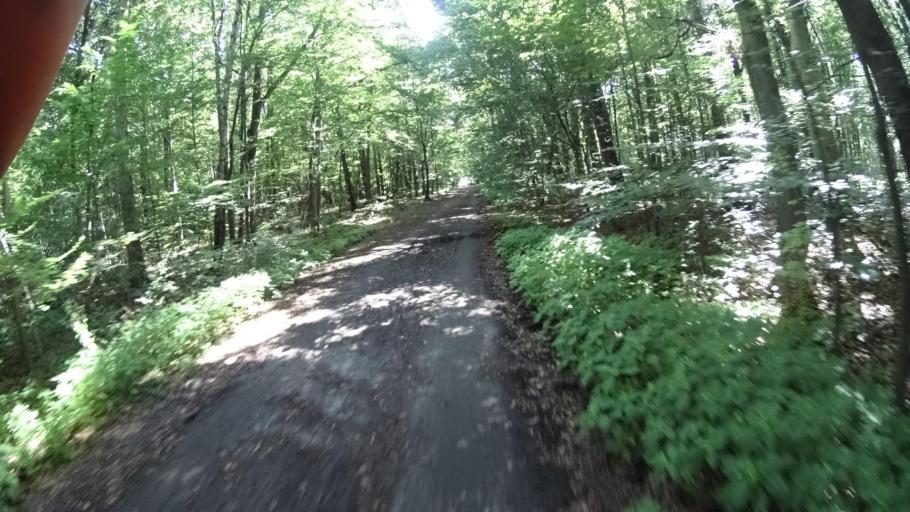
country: PL
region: Masovian Voivodeship
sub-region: Powiat piaseczynski
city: Jozefoslaw
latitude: 52.1113
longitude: 21.0554
